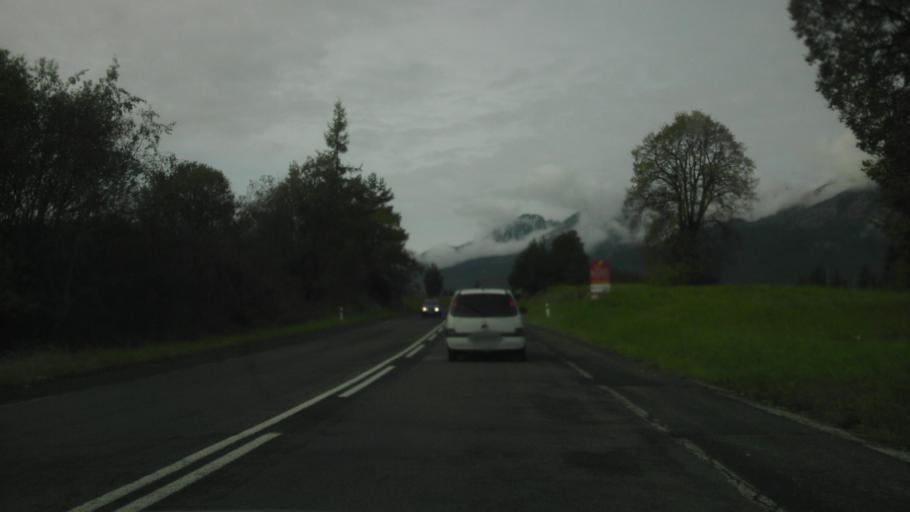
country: SK
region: Presovsky
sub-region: Okres Poprad
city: Nova Lesna
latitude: 49.1161
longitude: 20.2599
